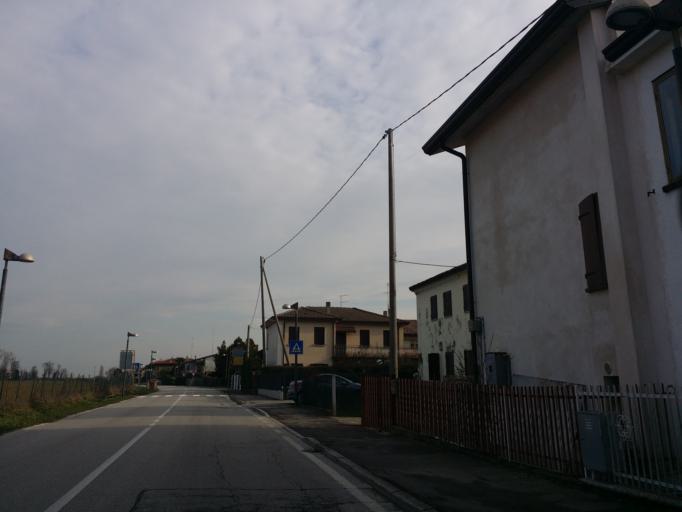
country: IT
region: Veneto
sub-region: Provincia di Padova
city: Terradura
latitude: 45.3502
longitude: 11.8195
